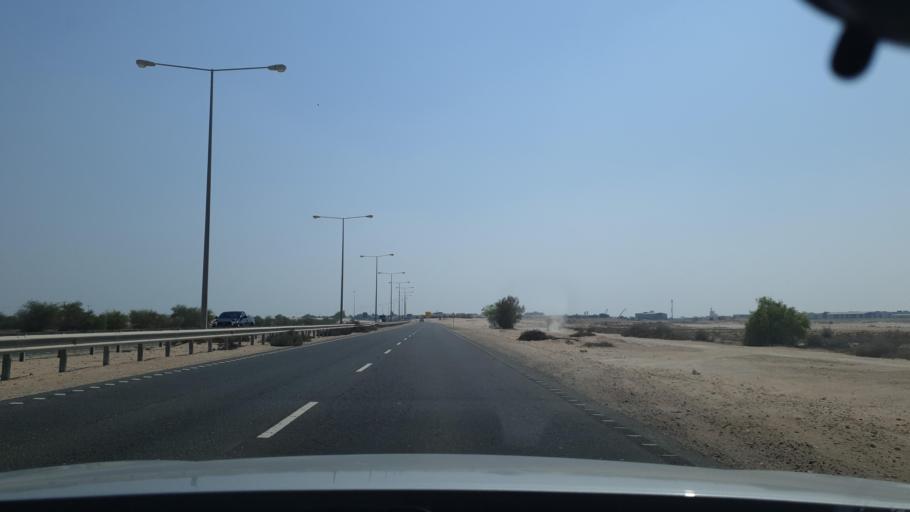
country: QA
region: Al Khawr
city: Al Khawr
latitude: 25.7275
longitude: 51.4960
